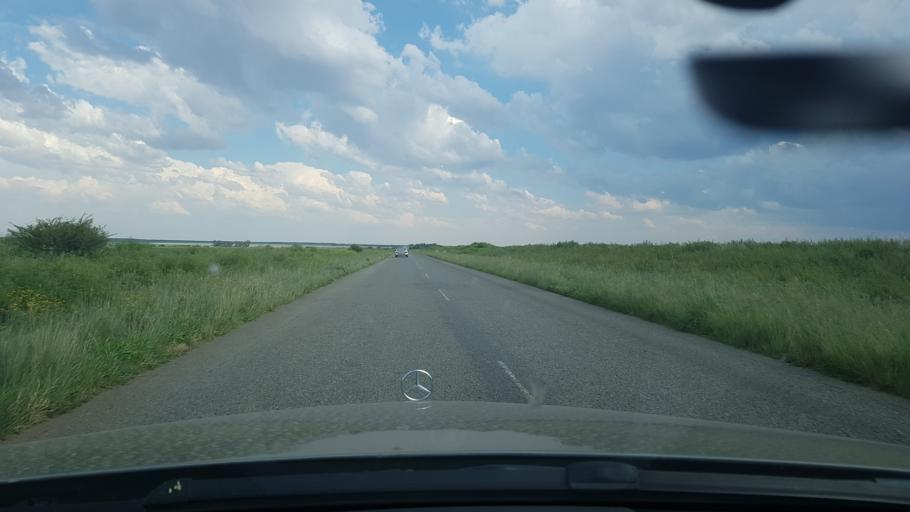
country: ZA
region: North-West
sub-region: Dr Ruth Segomotsi Mompati District Municipality
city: Bloemhof
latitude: -27.8357
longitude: 25.6391
